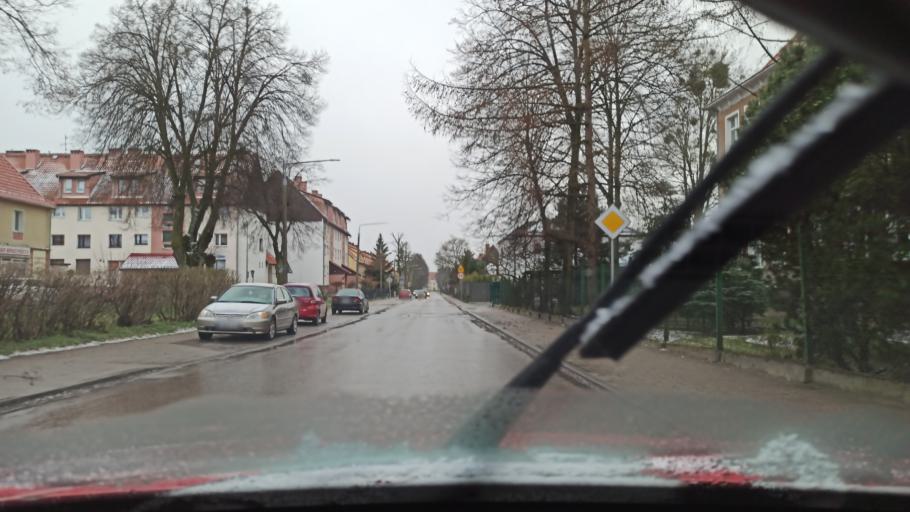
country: PL
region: Warmian-Masurian Voivodeship
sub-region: Powiat elblaski
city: Elblag
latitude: 54.1779
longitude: 19.4131
